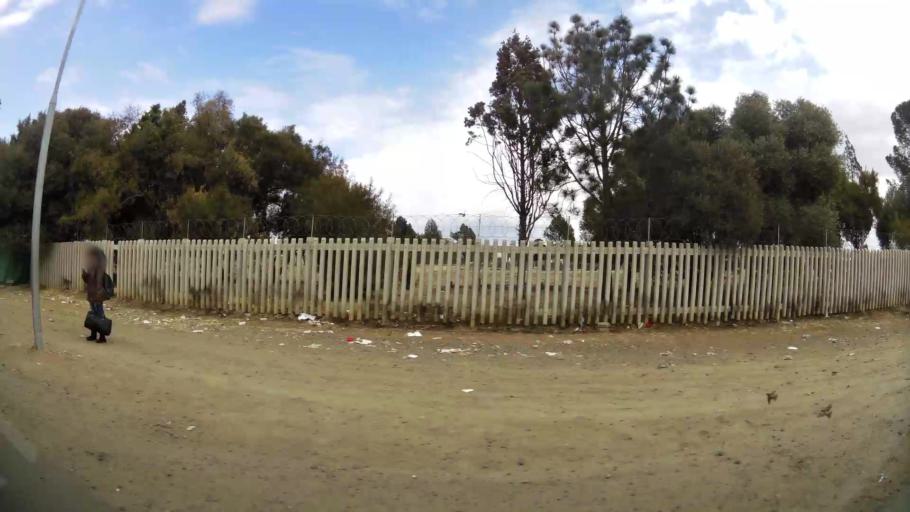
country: ZA
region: Orange Free State
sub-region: Fezile Dabi District Municipality
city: Kroonstad
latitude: -27.6423
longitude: 27.2212
